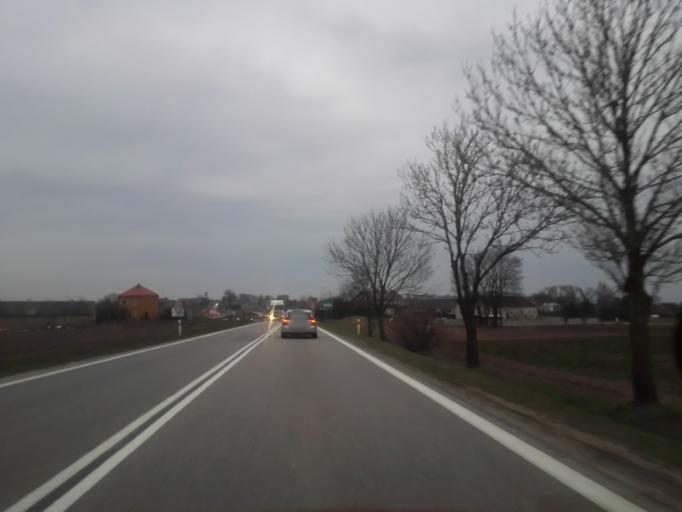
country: PL
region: Podlasie
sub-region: Powiat lomzynski
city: Piatnica
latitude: 53.2567
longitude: 22.1226
